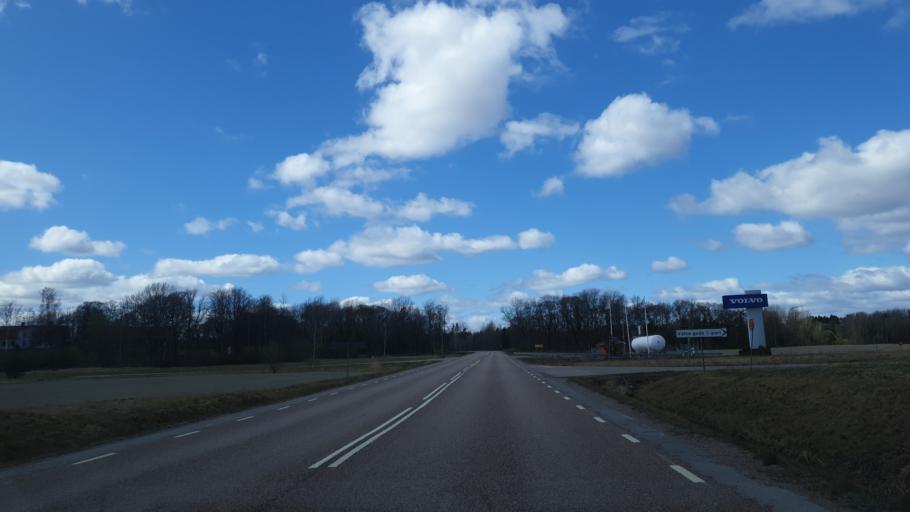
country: SE
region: Vaestmanland
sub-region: Kopings Kommun
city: Koping
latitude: 59.4980
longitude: 15.9849
